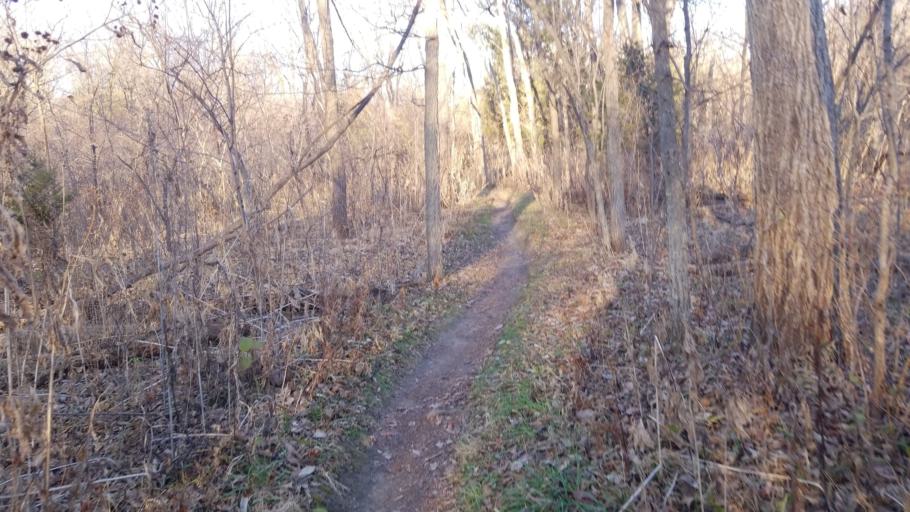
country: US
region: Nebraska
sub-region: Sarpy County
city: Offutt Air Force Base
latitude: 41.1662
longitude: -95.9605
